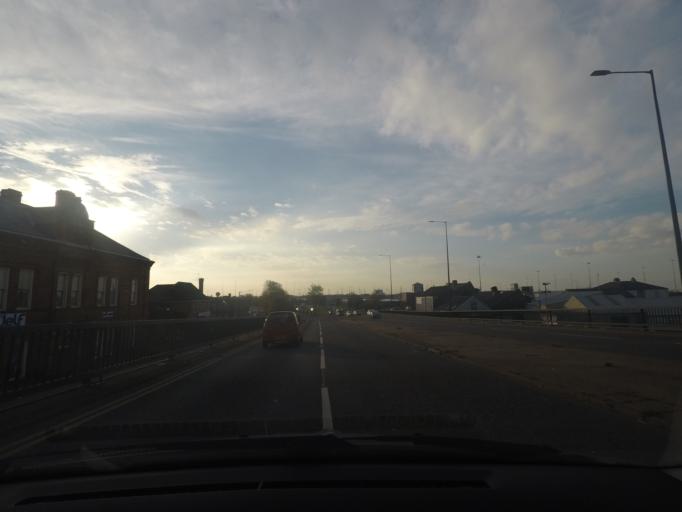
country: GB
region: England
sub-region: North East Lincolnshire
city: Grimsby
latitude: 53.5751
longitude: -0.0764
